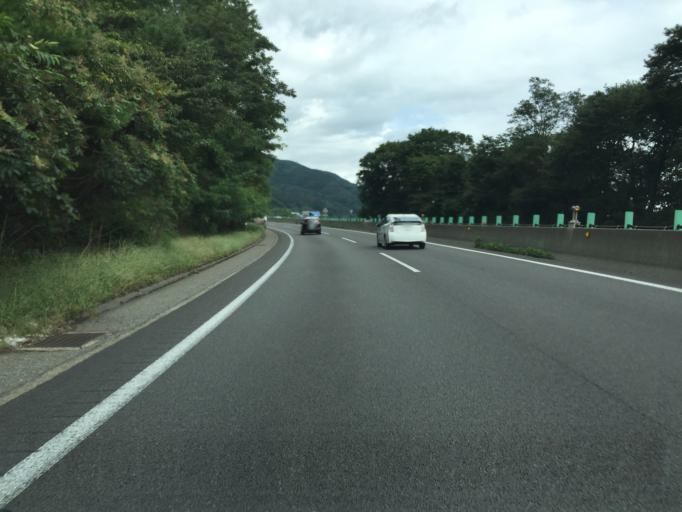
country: JP
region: Fukushima
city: Yanagawamachi-saiwaicho
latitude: 37.8930
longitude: 140.5690
